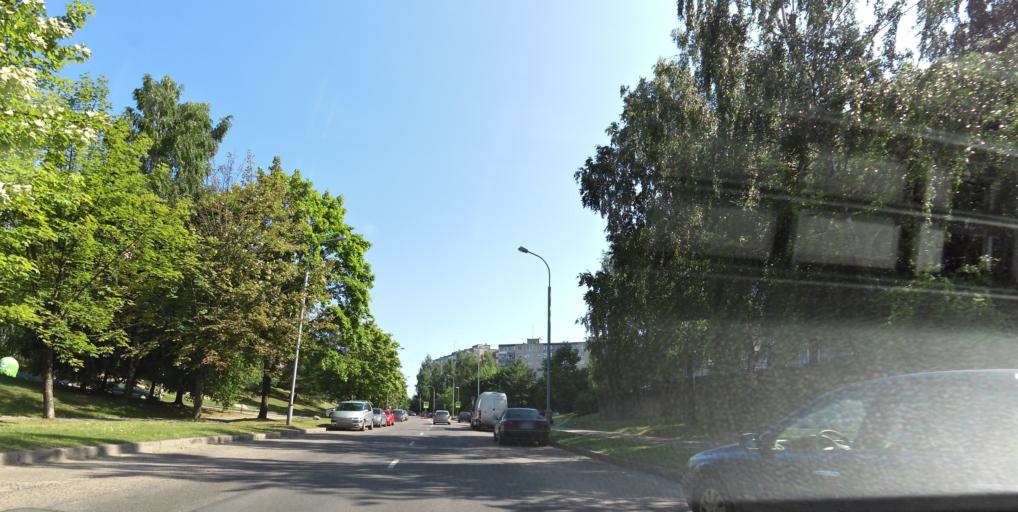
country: LT
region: Vilnius County
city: Justiniskes
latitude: 54.7101
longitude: 25.2215
